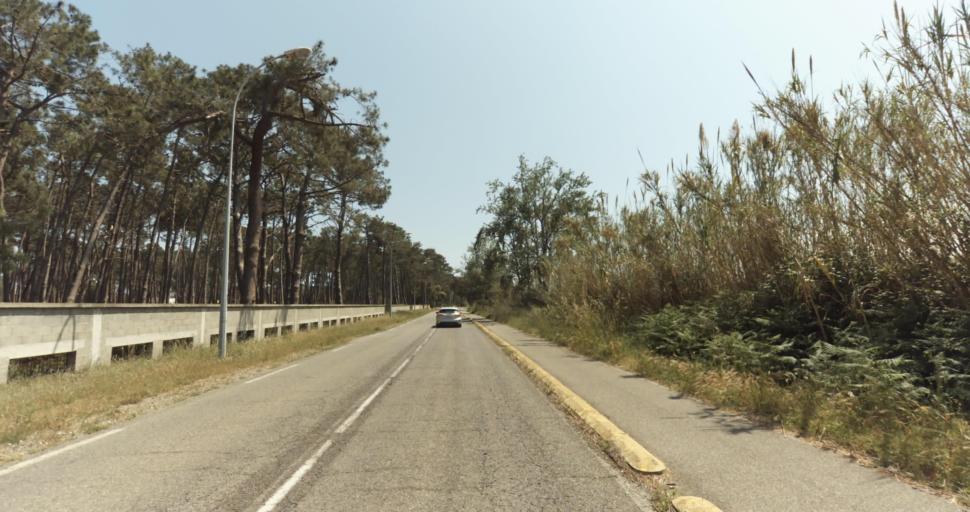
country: FR
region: Corsica
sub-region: Departement de la Haute-Corse
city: Biguglia
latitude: 42.6203
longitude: 9.4747
